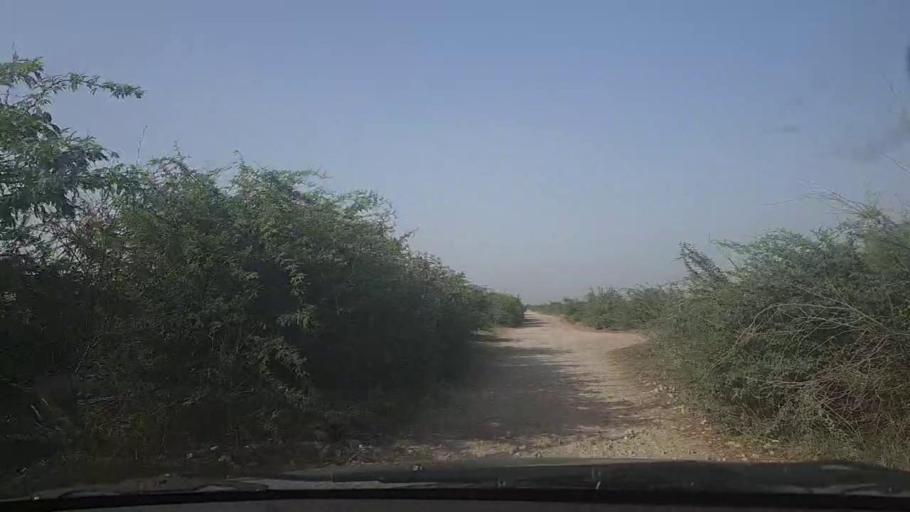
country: PK
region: Sindh
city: Keti Bandar
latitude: 24.2506
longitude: 67.5612
